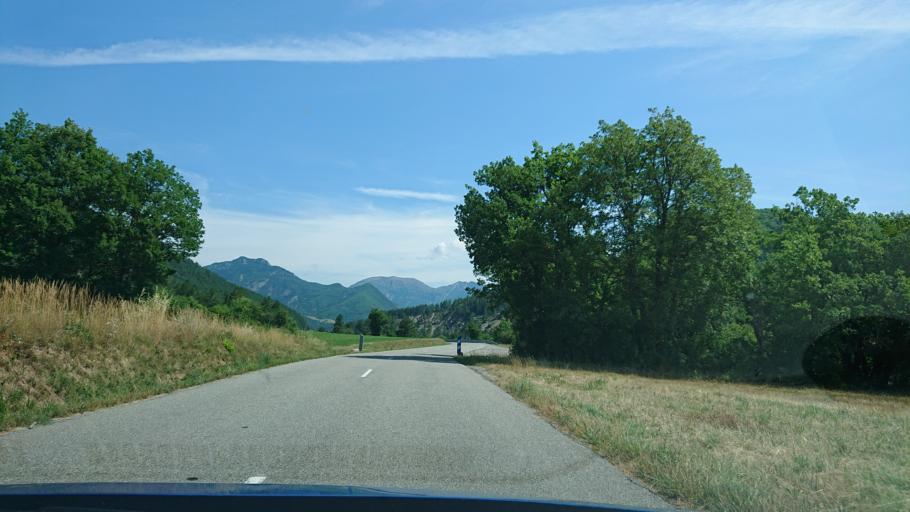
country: FR
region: Provence-Alpes-Cote d'Azur
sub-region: Departement des Alpes-de-Haute-Provence
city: Sisteron
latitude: 44.2873
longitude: 6.0234
